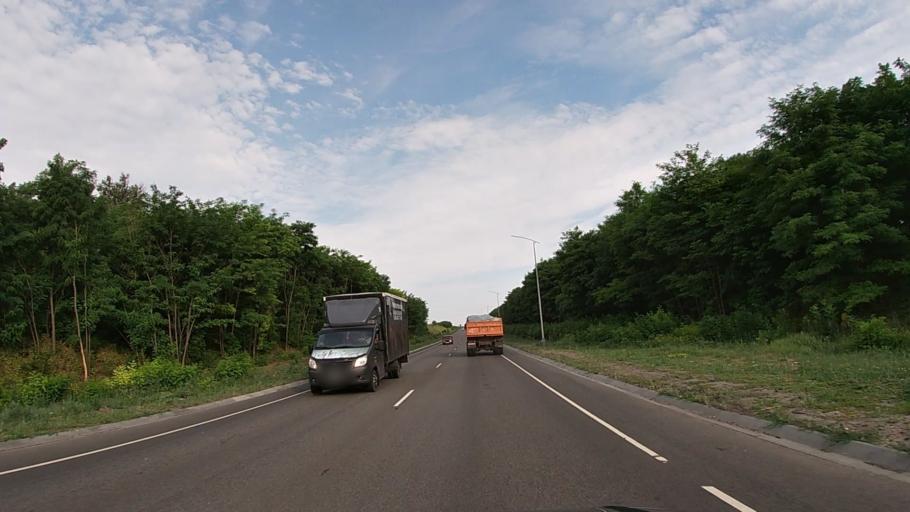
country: RU
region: Belgorod
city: Severnyy
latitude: 50.6686
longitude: 36.4897
